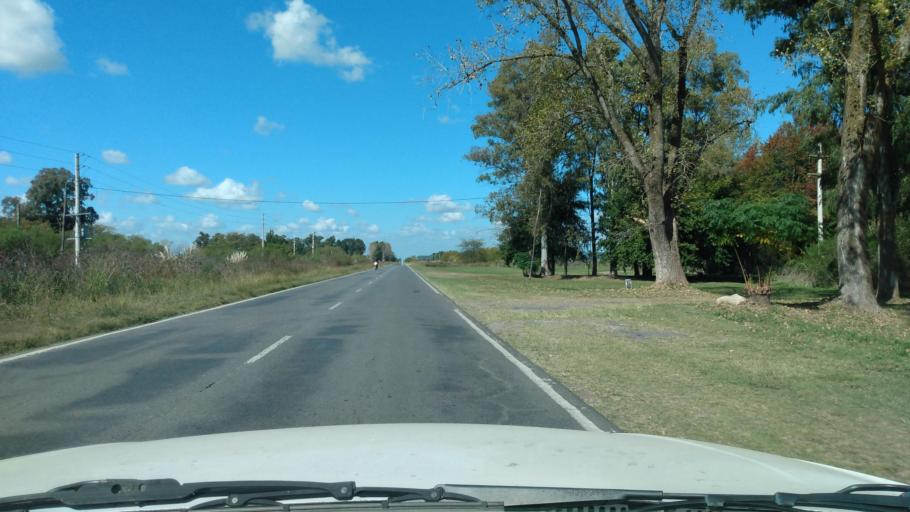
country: AR
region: Buenos Aires
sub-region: Partido de Mercedes
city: Mercedes
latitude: -34.7088
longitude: -59.4002
